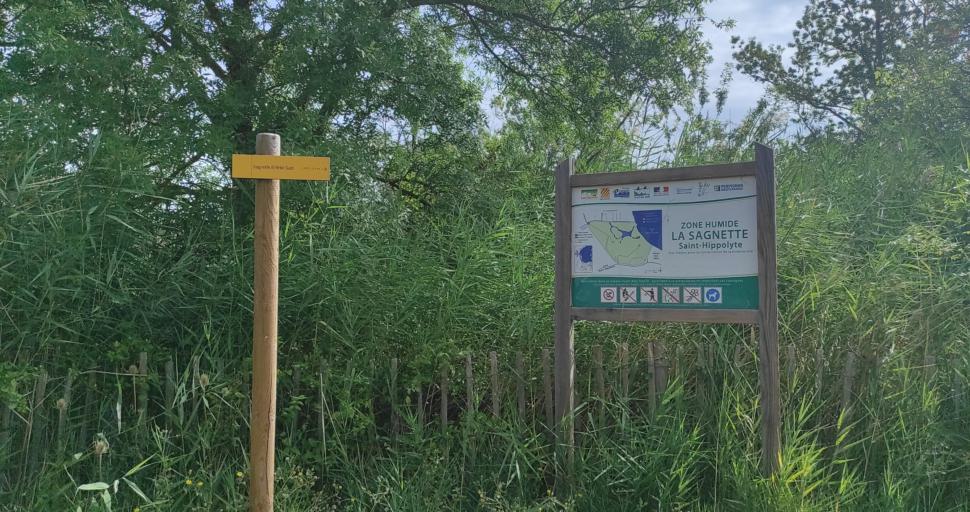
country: FR
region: Languedoc-Roussillon
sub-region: Departement des Pyrenees-Orientales
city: Saint-Hippolyte
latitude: 42.8051
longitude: 2.9708
